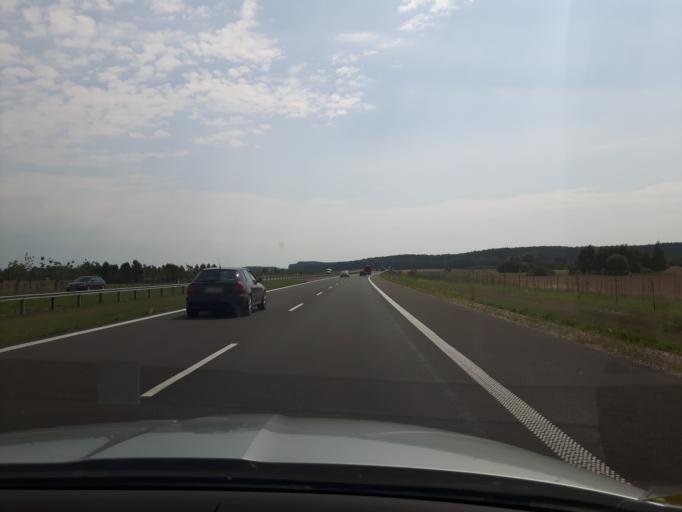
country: PL
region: Warmian-Masurian Voivodeship
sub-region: Powiat nidzicki
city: Nidzica
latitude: 53.3882
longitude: 20.3693
